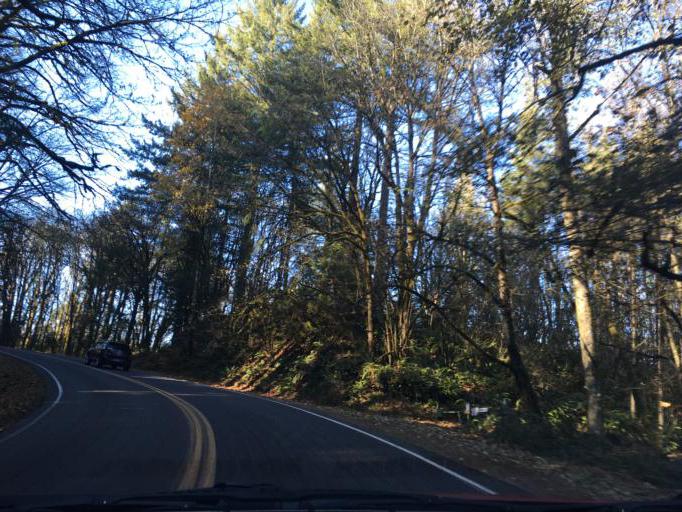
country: US
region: Oregon
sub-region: Washington County
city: Cedar Mill
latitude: 45.5896
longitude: -122.7906
